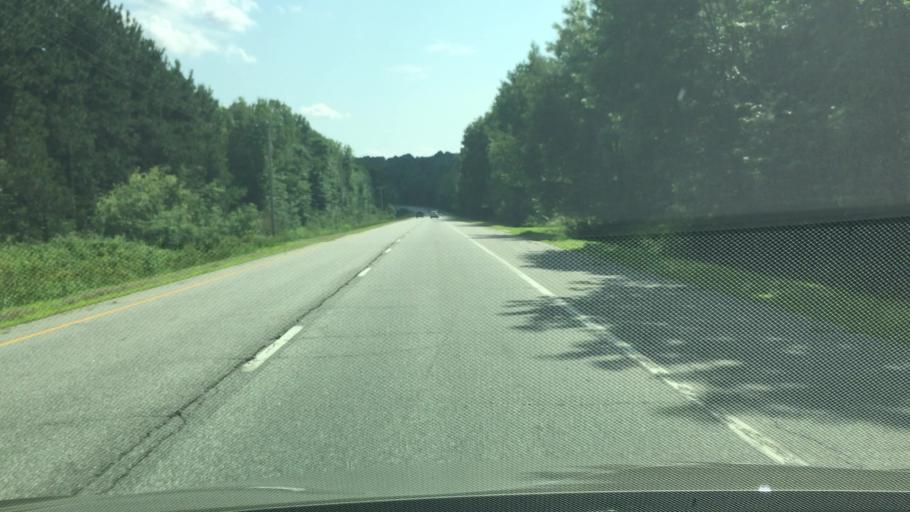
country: US
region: Maine
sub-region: Androscoggin County
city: Auburn
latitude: 44.0635
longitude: -70.2529
